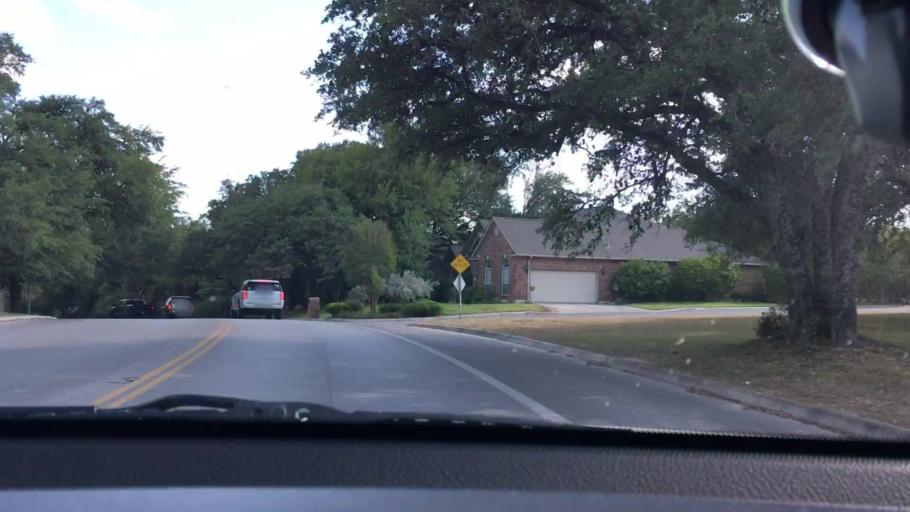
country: US
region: Texas
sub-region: Bexar County
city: Live Oak
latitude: 29.5737
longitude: -98.3213
